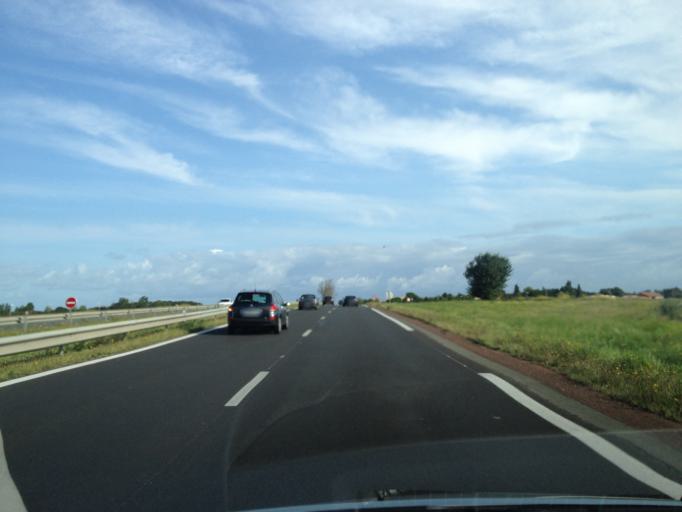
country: FR
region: Poitou-Charentes
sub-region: Departement de la Charente-Maritime
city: Yves
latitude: 46.0135
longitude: -1.0494
